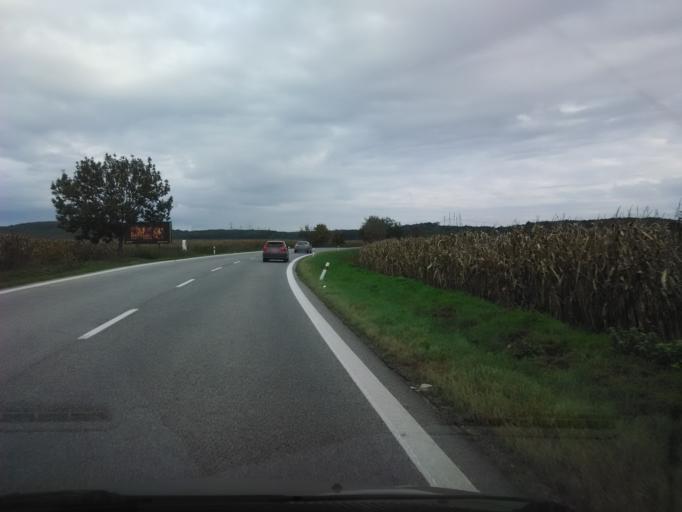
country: SK
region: Nitriansky
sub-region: Okres Nitra
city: Vrable
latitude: 48.2313
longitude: 18.4035
